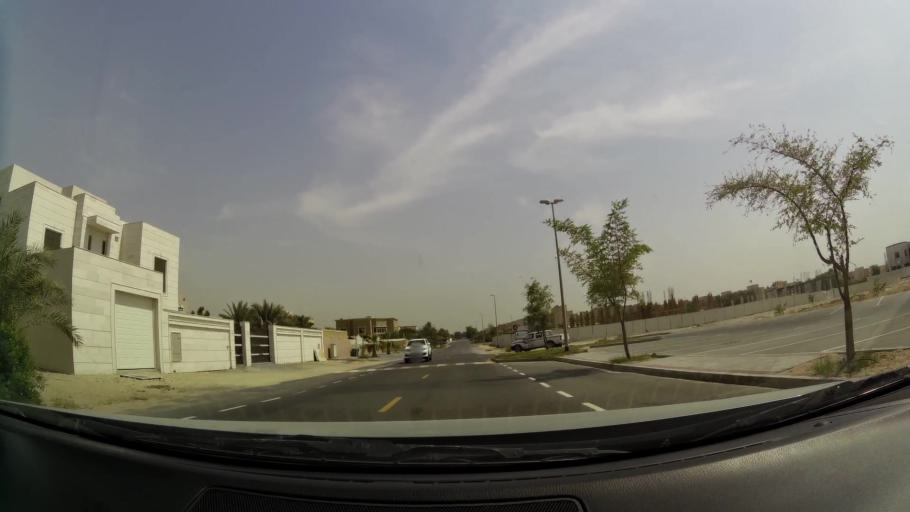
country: AE
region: Ash Shariqah
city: Sharjah
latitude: 25.2372
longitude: 55.4451
